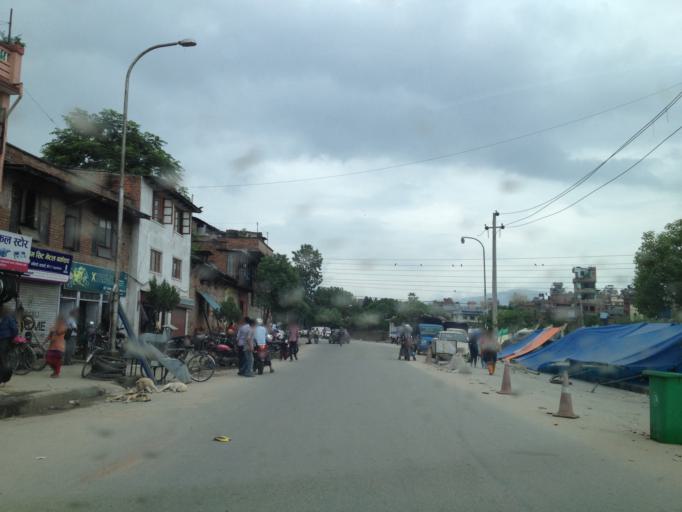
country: NP
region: Central Region
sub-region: Bagmati Zone
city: Kathmandu
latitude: 27.6996
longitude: 85.3024
